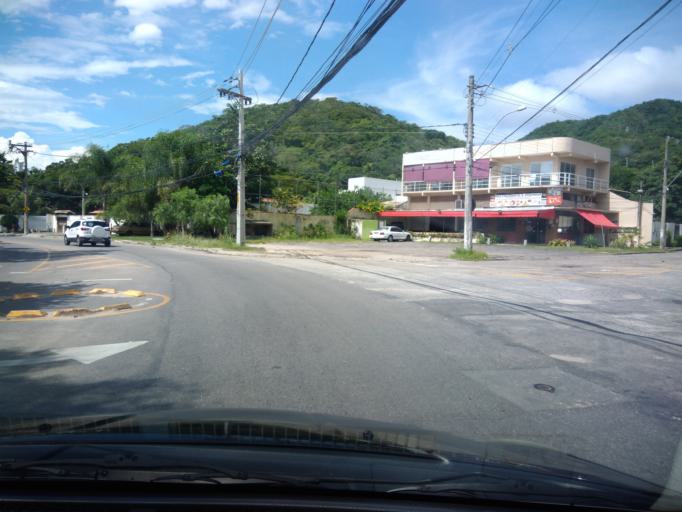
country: BR
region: Rio de Janeiro
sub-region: Niteroi
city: Niteroi
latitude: -22.9520
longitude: -43.0252
